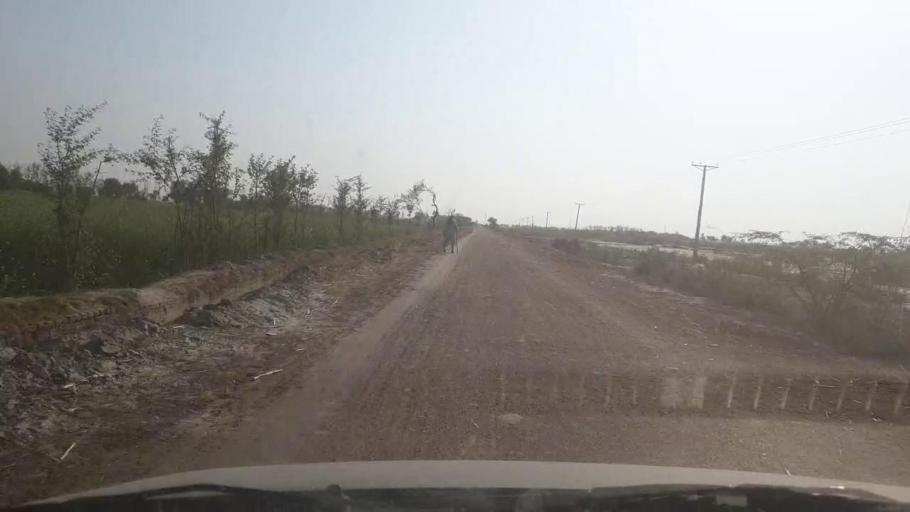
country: PK
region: Sindh
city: Samaro
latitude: 25.1505
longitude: 69.3821
